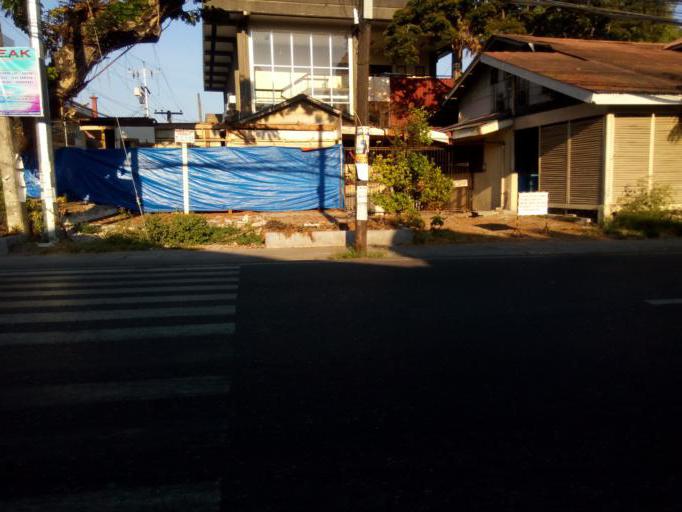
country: PH
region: Central Visayas
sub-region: Province of Negros Oriental
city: Dumaguete
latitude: 9.3117
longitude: 123.3074
